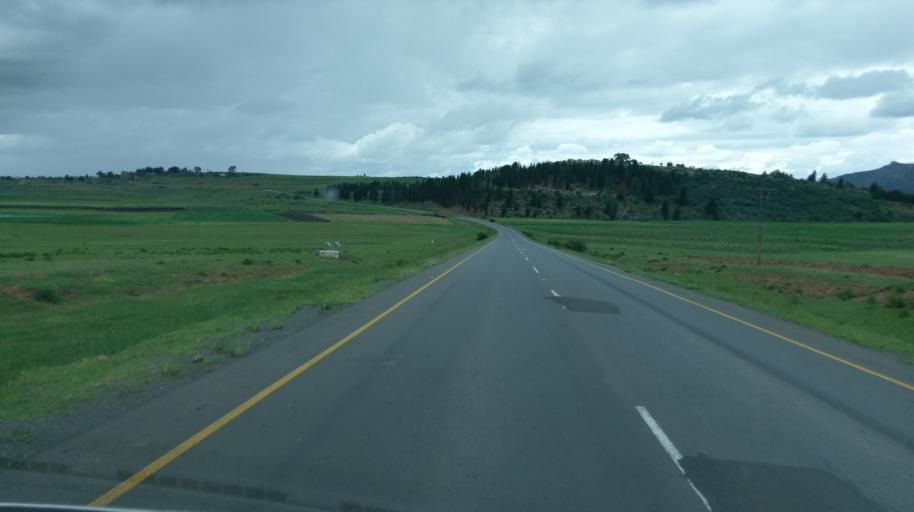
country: LS
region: Maseru
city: Maseru
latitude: -29.5272
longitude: 27.5184
